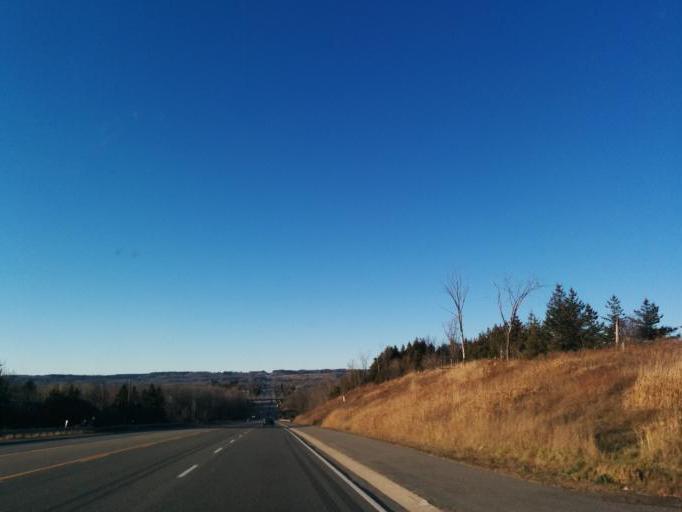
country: CA
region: Ontario
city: Brampton
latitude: 43.8070
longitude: -79.9237
